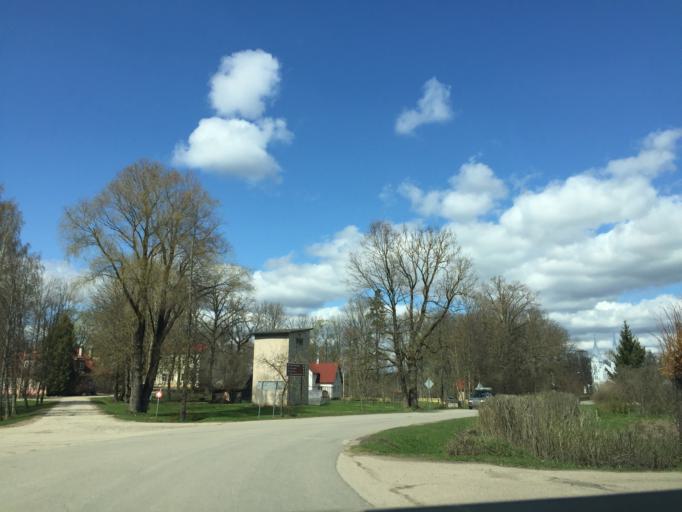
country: LV
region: Vilanu
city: Vilani
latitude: 56.7339
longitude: 27.0672
